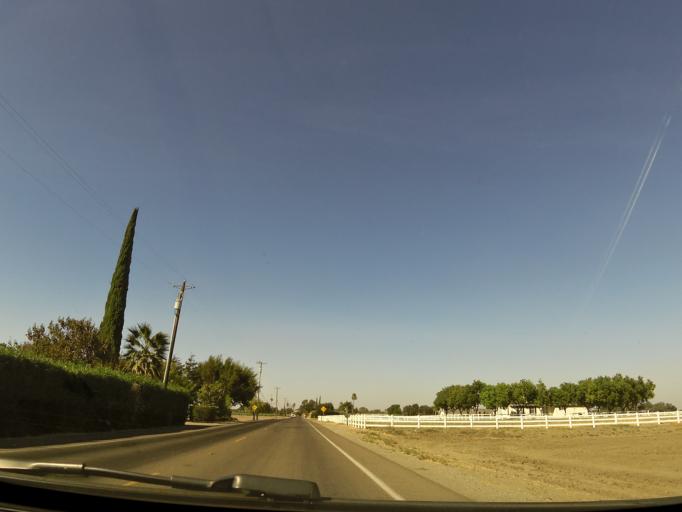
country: US
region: California
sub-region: San Joaquin County
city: Tracy
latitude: 37.7853
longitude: -121.4352
